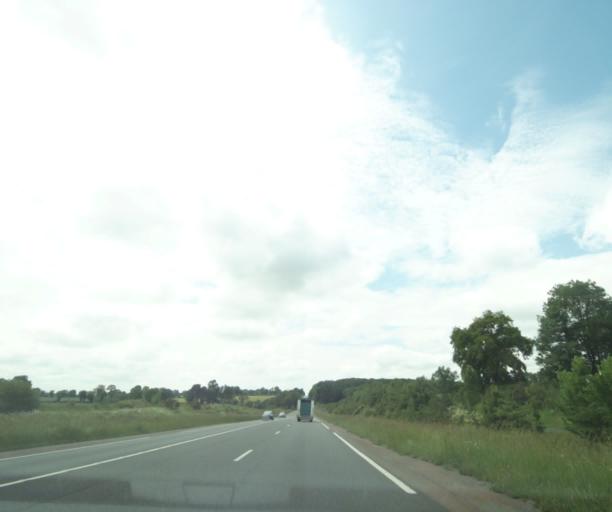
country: FR
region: Poitou-Charentes
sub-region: Departement des Deux-Sevres
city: Saint-Pardoux
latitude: 46.5133
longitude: -0.3314
